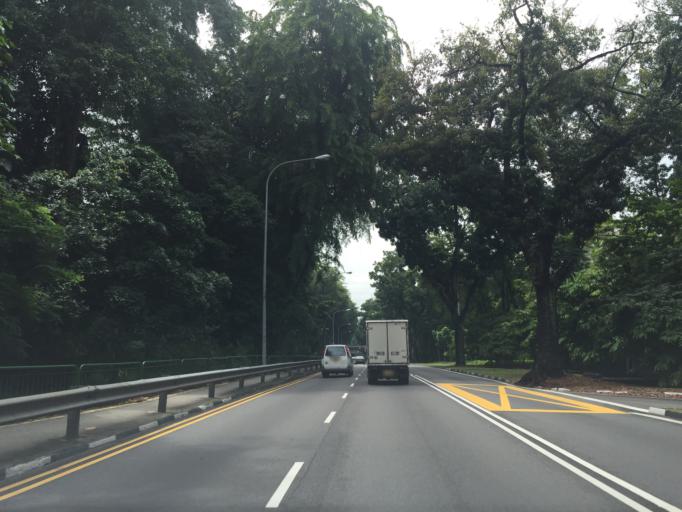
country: SG
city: Singapore
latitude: 1.3196
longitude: 103.8302
